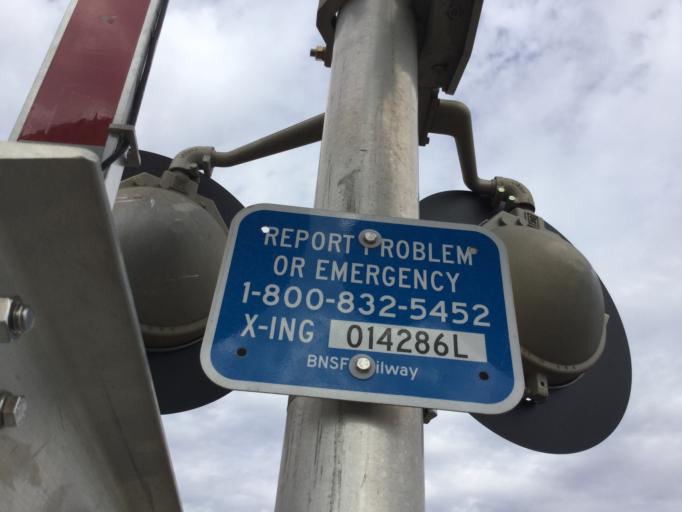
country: US
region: Kansas
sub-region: Barber County
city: Kiowa
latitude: 37.0652
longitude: -98.4400
